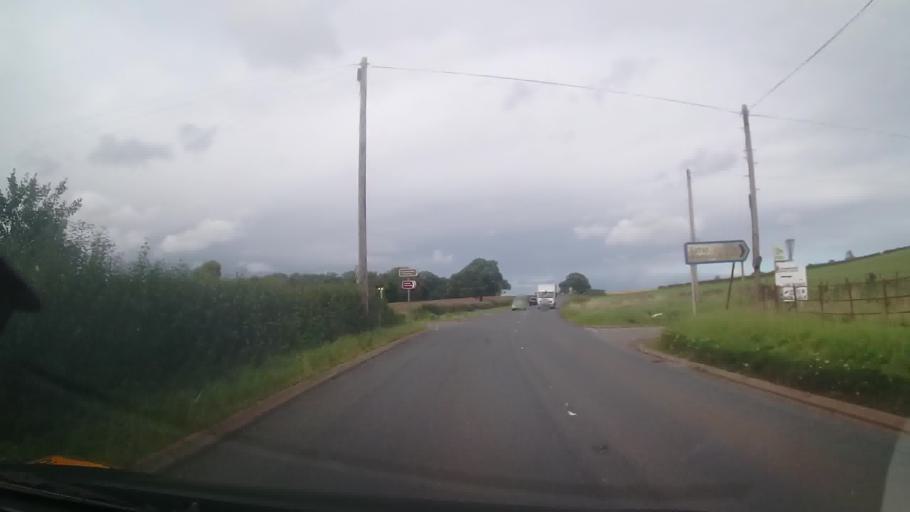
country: GB
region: England
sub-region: Shropshire
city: Alveley
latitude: 52.4746
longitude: -2.3530
